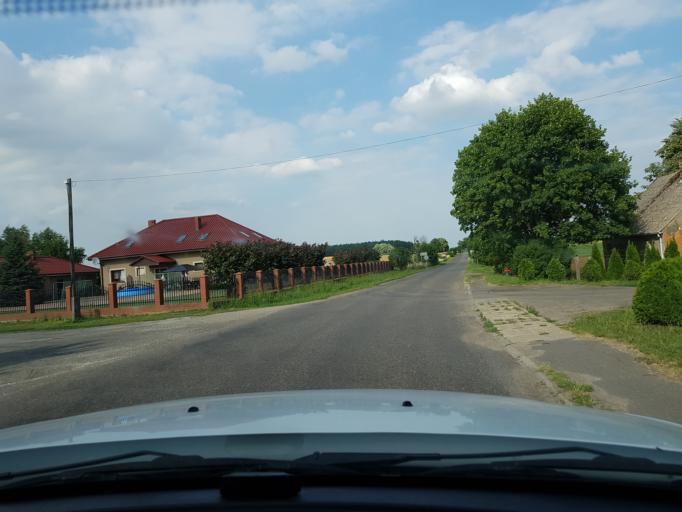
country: PL
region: West Pomeranian Voivodeship
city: Trzcinsko Zdroj
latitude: 53.0084
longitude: 14.5260
